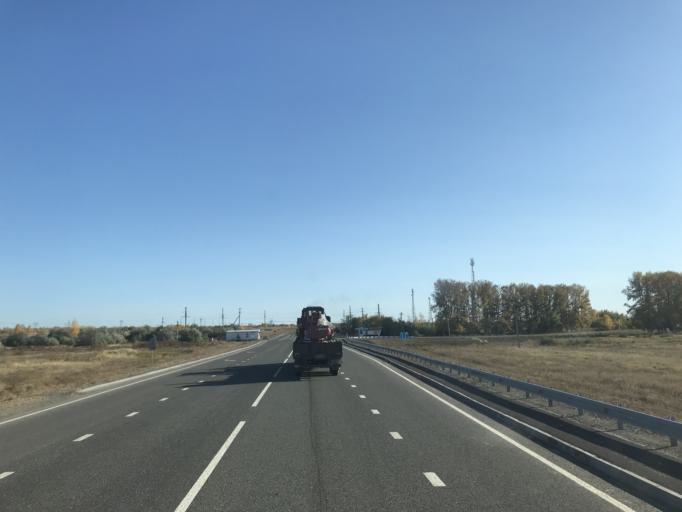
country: KZ
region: Pavlodar
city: Koktobe
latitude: 51.9274
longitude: 77.3327
